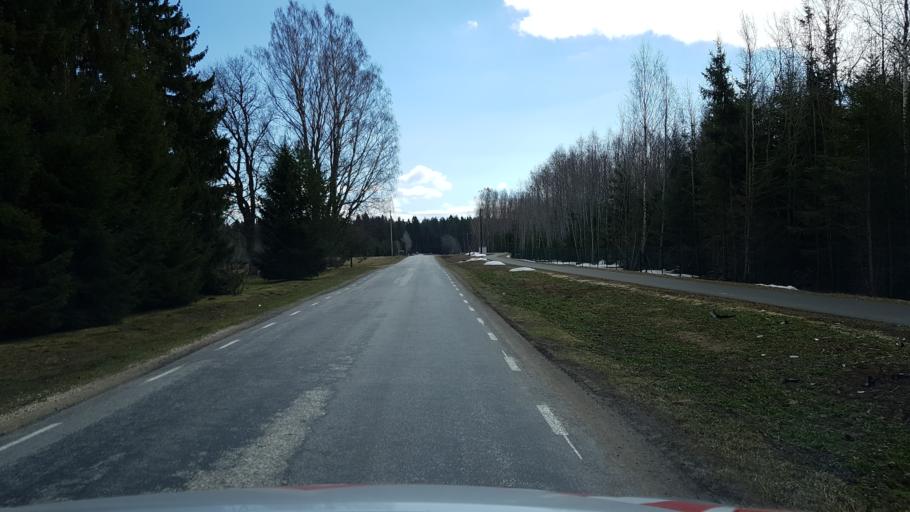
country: EE
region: Laeaene-Virumaa
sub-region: Haljala vald
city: Haljala
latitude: 59.3908
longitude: 26.2919
